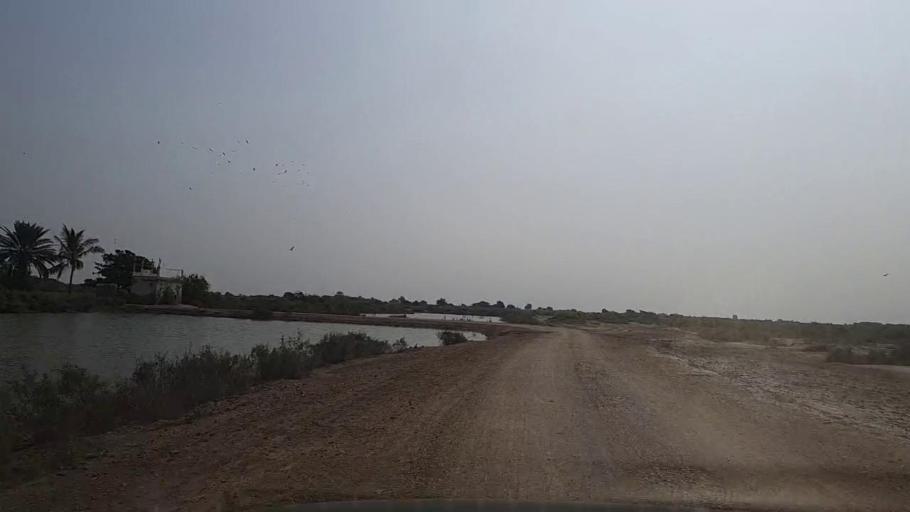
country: PK
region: Sindh
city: Thatta
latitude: 24.5698
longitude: 67.9173
